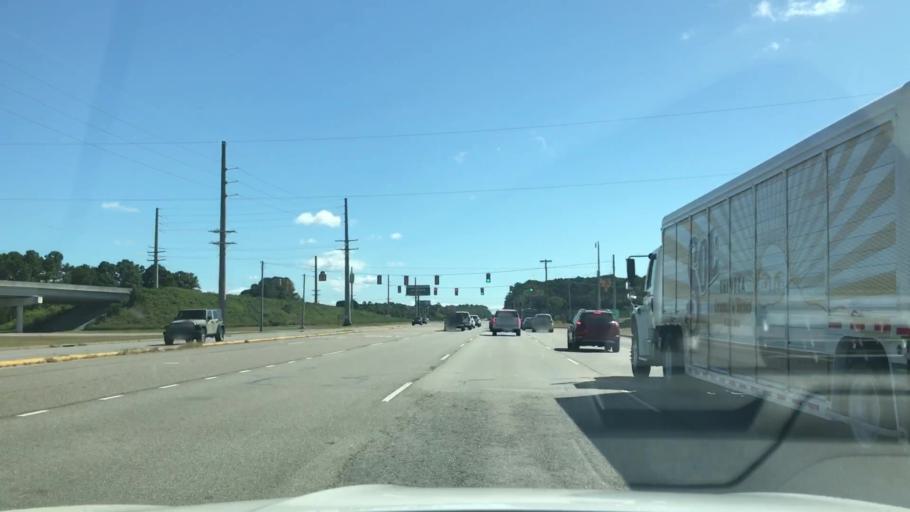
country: US
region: South Carolina
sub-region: Horry County
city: North Myrtle Beach
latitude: 33.7873
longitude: -78.7747
